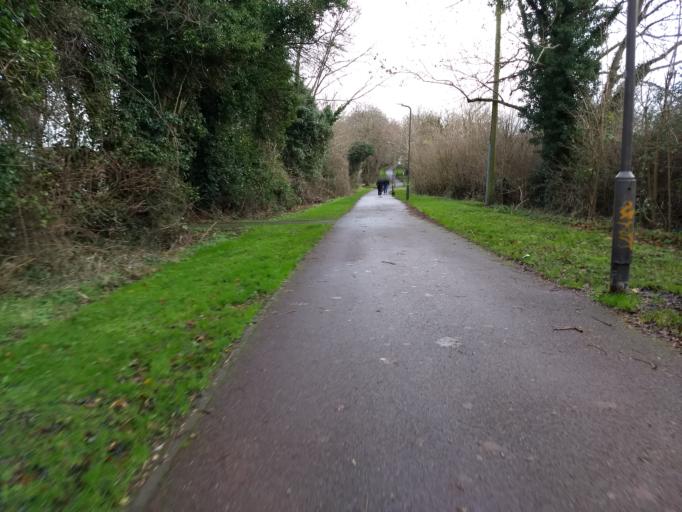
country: GB
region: England
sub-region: Buckinghamshire
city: Newton Longville
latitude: 51.9972
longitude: -0.7708
